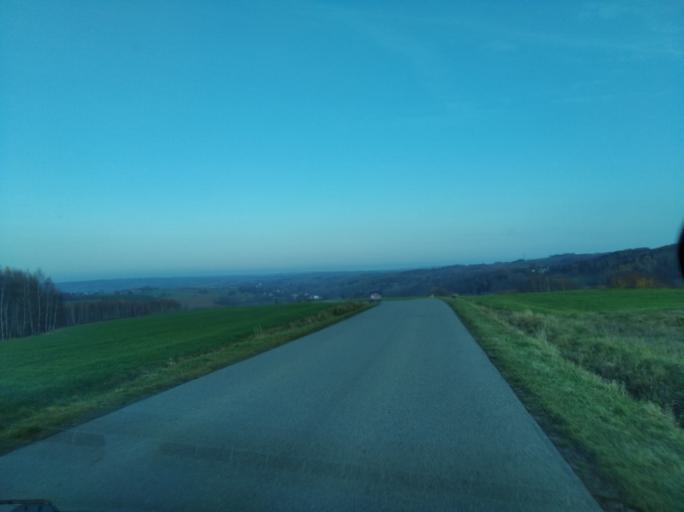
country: PL
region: Subcarpathian Voivodeship
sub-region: Powiat ropczycko-sedziszowski
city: Zagorzyce
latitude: 49.9862
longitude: 21.7177
